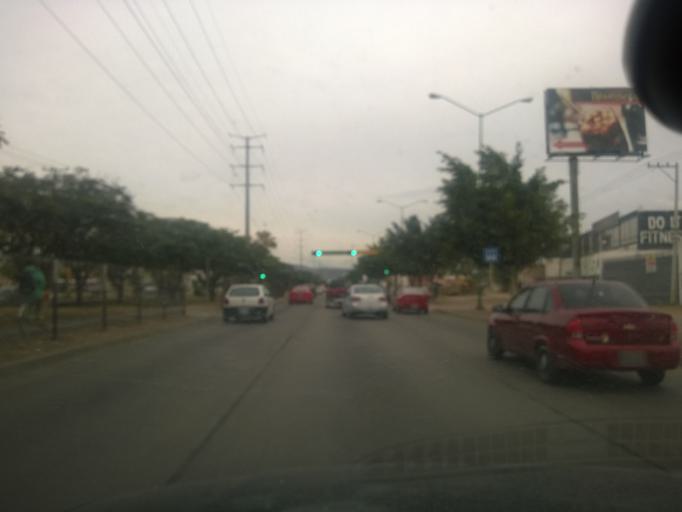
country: MX
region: Guanajuato
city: Leon
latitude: 21.1457
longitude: -101.6494
